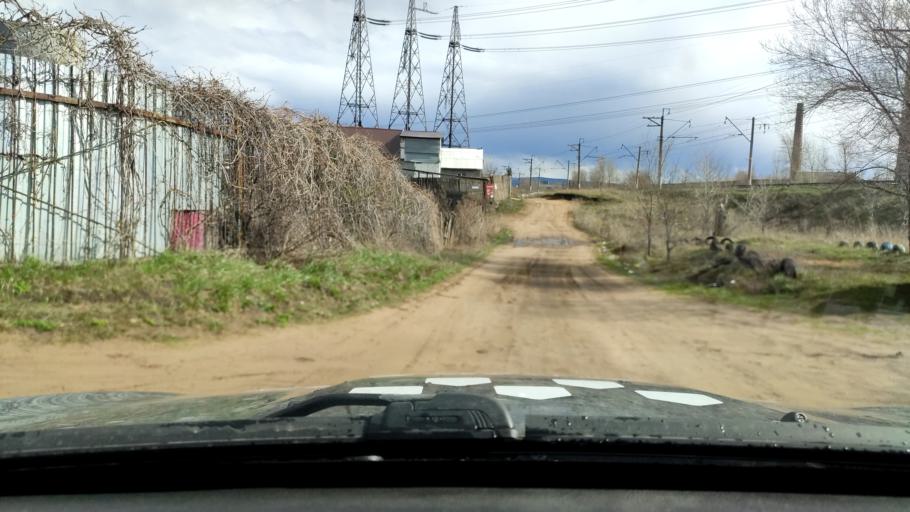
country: RU
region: Samara
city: Zhigulevsk
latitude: 53.4924
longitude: 49.4927
